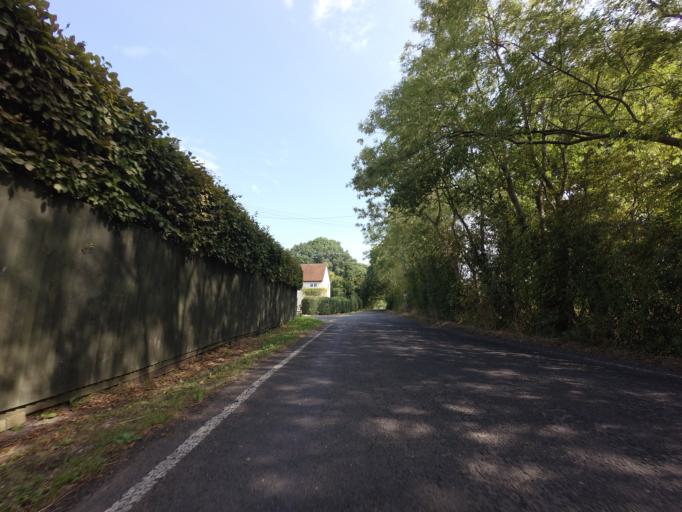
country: GB
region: England
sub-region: Kent
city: Staplehurst
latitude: 51.1306
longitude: 0.5794
